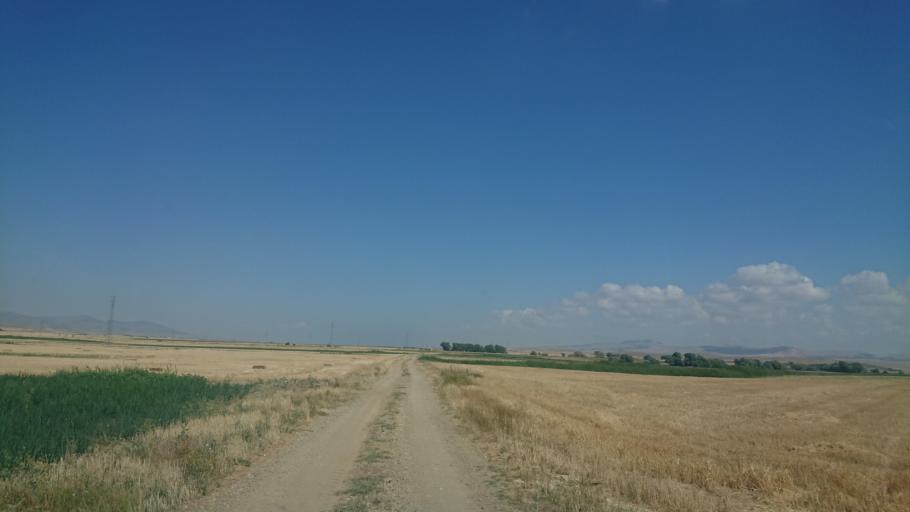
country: TR
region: Aksaray
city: Sariyahsi
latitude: 38.9896
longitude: 33.9012
